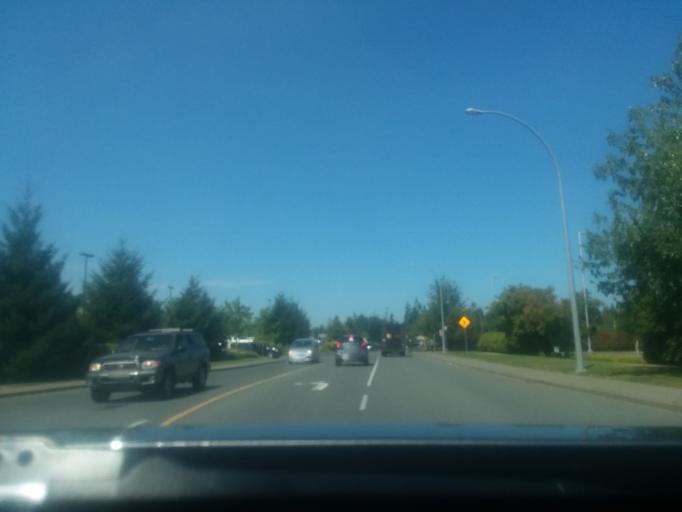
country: CA
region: British Columbia
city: Courtenay
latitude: 49.7134
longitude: -124.9620
